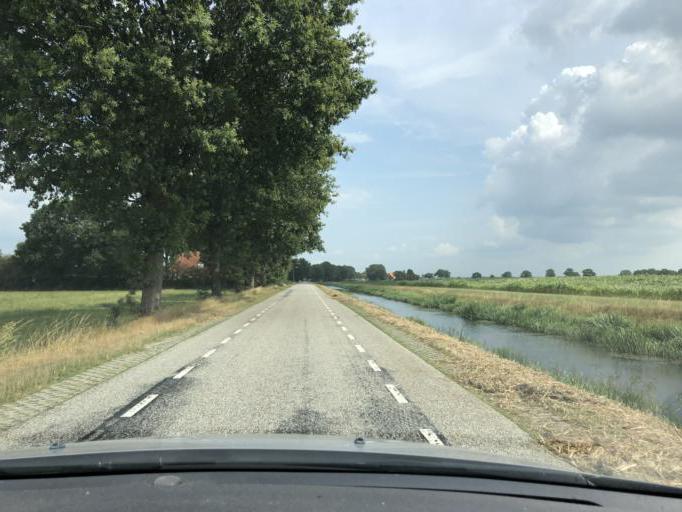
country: NL
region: Drenthe
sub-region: Gemeente Coevorden
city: Dalen
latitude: 52.7828
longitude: 6.6265
